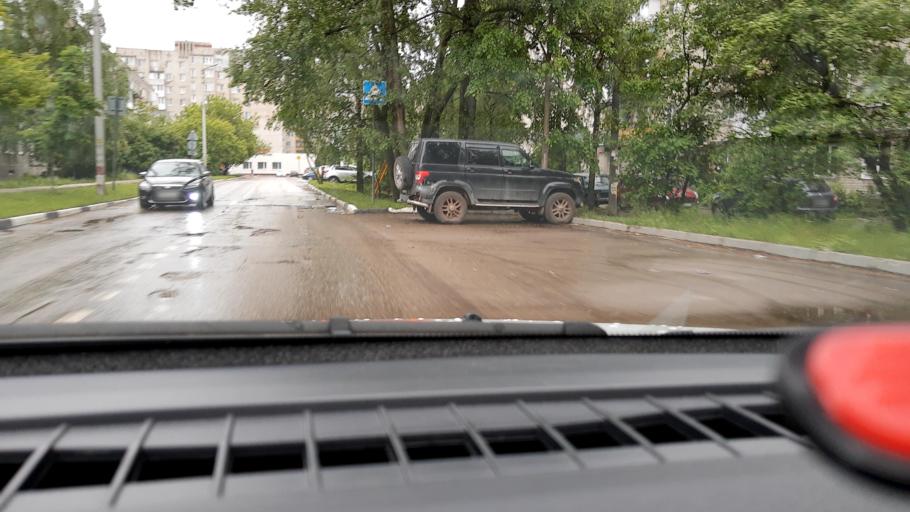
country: RU
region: Nizjnij Novgorod
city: Bor
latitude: 56.3543
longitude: 44.0683
